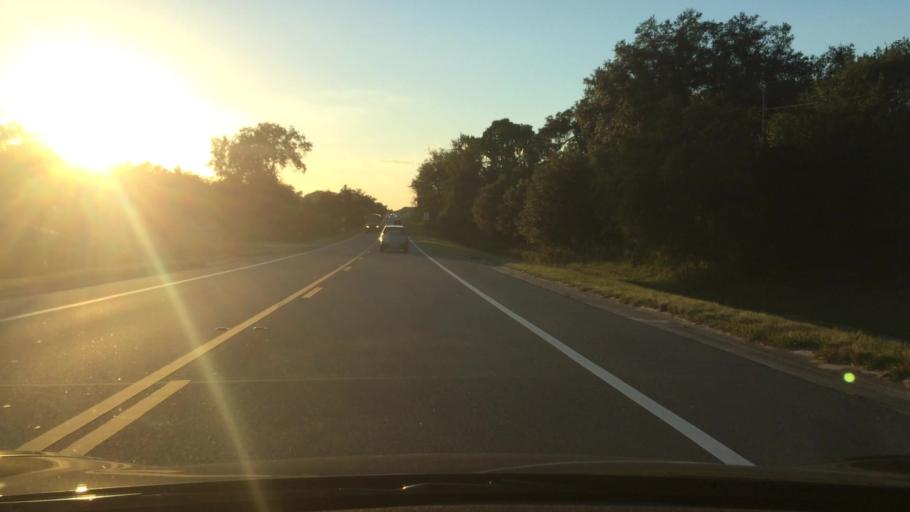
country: US
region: Florida
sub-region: Hillsborough County
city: Pebble Creek
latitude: 28.1713
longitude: -82.3964
